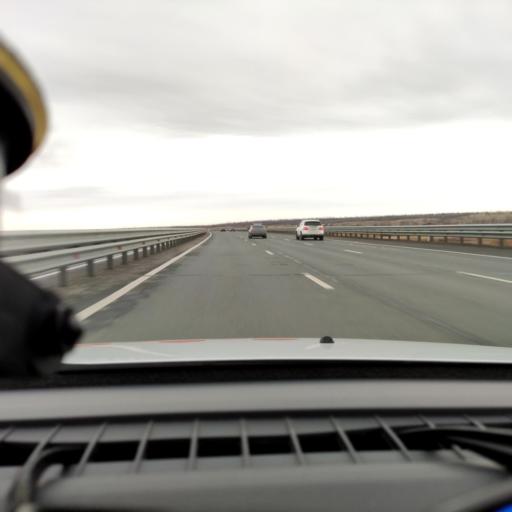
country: RU
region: Samara
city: Smyshlyayevka
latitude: 53.1605
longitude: 50.3281
